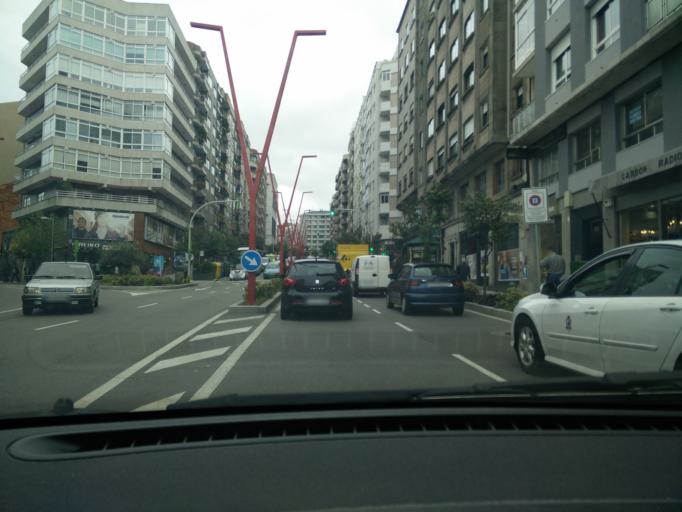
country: ES
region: Galicia
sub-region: Provincia de Pontevedra
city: Vigo
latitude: 42.2216
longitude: -8.7320
